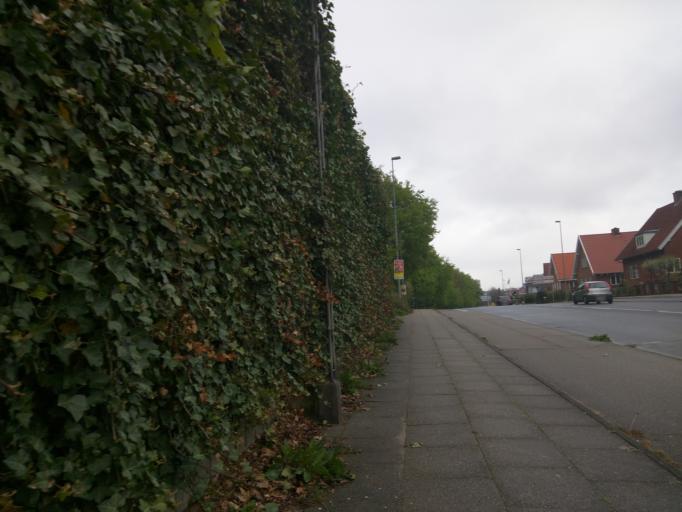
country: DK
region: Central Jutland
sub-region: Viborg Kommune
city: Viborg
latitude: 56.4406
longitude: 9.4030
